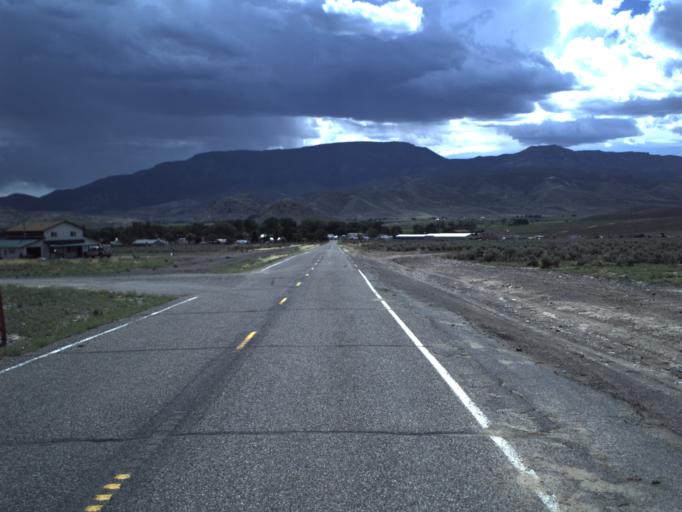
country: US
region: Utah
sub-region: Piute County
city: Junction
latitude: 38.2443
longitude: -112.2330
